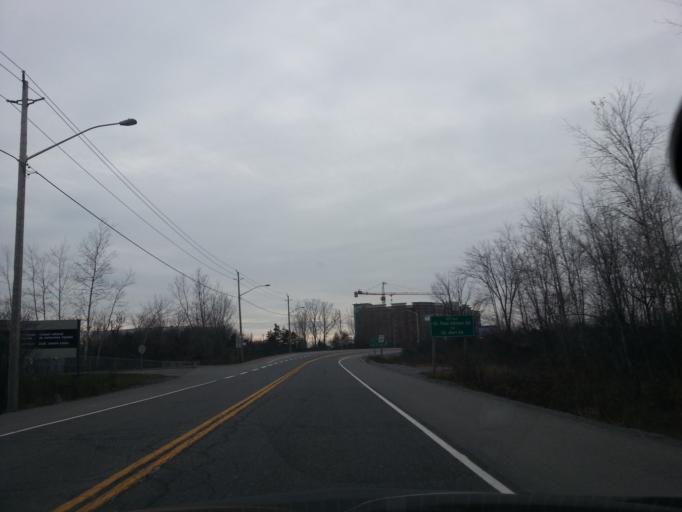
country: CA
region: Ontario
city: Ottawa
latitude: 45.3307
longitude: -75.6483
